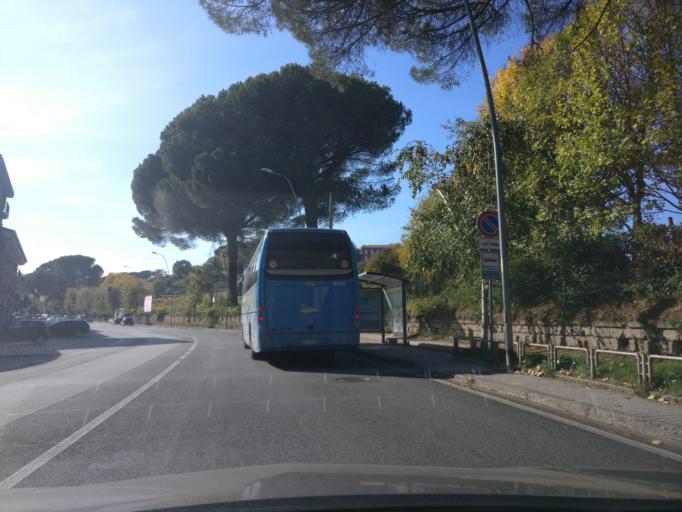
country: IT
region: Campania
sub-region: Provincia di Avellino
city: Torelli-Torrette
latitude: 40.9116
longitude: 14.7714
